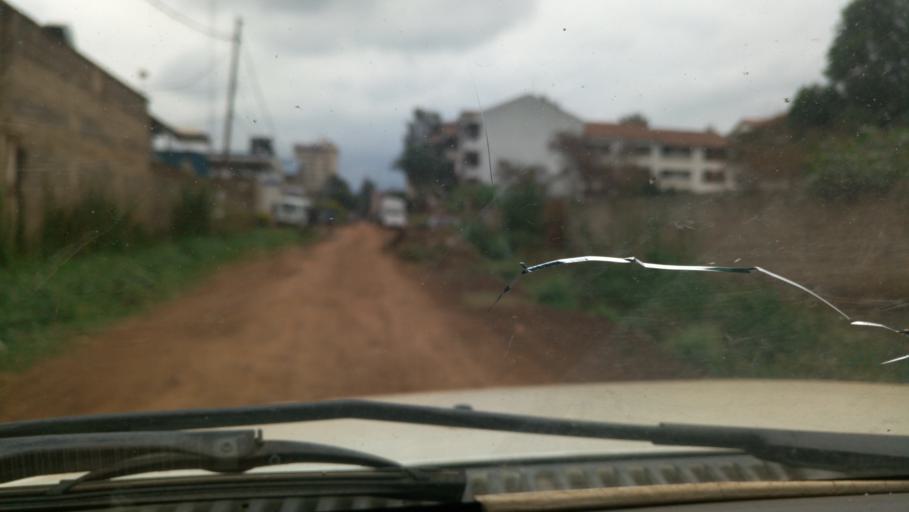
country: KE
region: Nairobi Area
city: Pumwani
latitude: -1.2264
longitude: 36.8820
